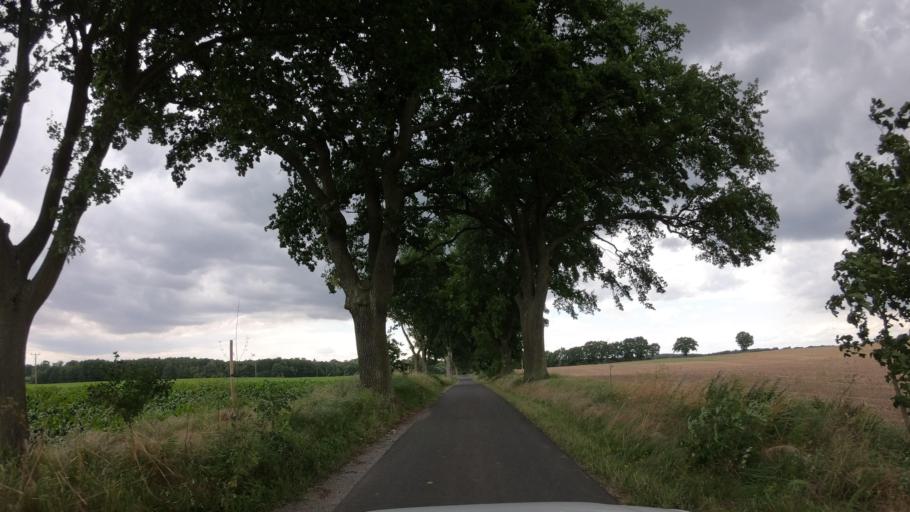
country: PL
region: West Pomeranian Voivodeship
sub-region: Powiat stargardzki
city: Suchan
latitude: 53.1869
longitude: 15.3080
